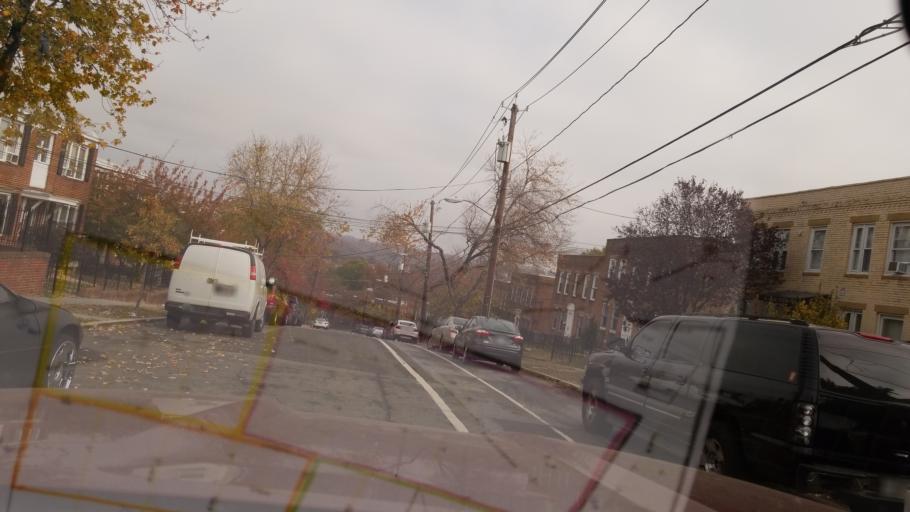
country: US
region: Maryland
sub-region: Prince George's County
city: Glassmanor
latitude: 38.8244
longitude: -77.0102
